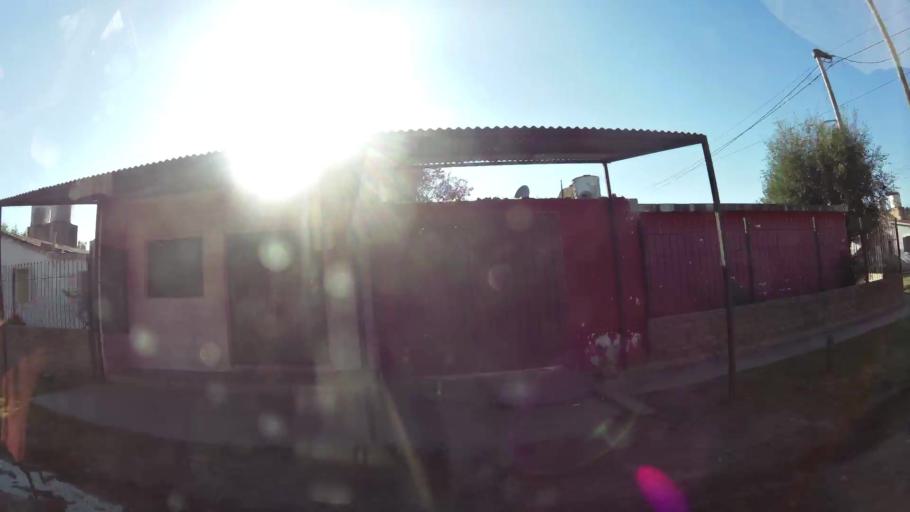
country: AR
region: Cordoba
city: Villa Allende
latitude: -31.3352
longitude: -64.2434
